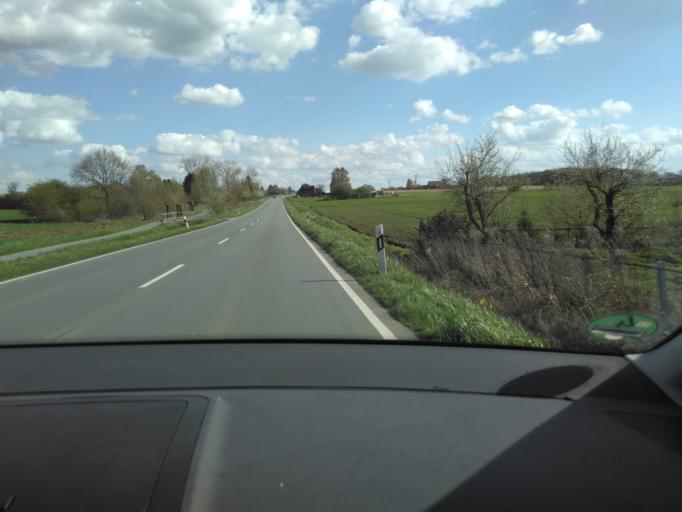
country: DE
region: North Rhine-Westphalia
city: Oelde
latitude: 51.7956
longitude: 8.1379
